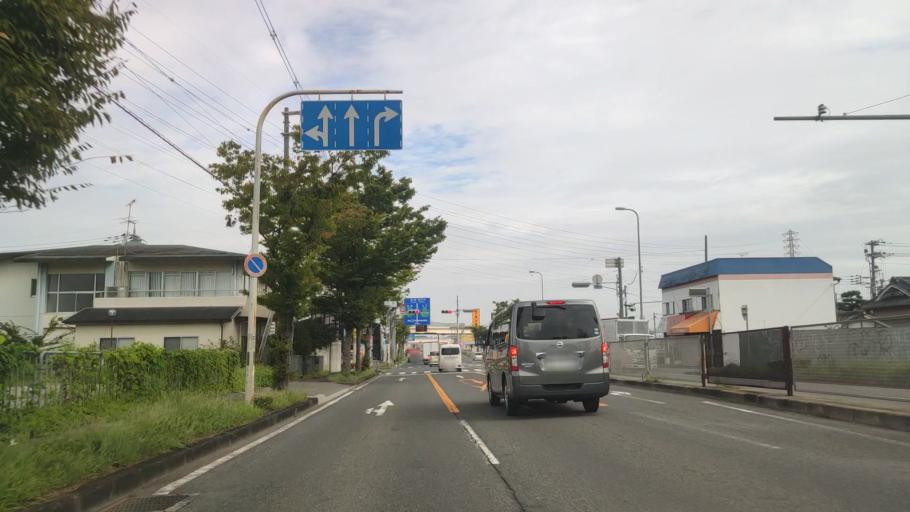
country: JP
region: Osaka
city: Tondabayashicho
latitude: 34.5299
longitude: 135.6049
